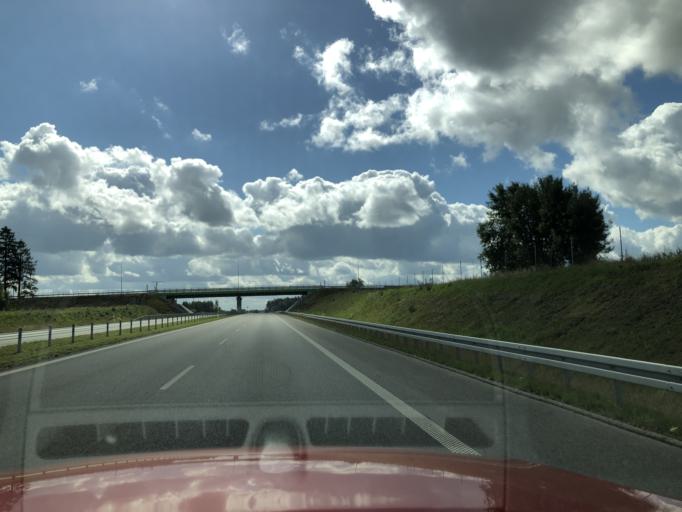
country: PL
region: West Pomeranian Voivodeship
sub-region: Powiat szczecinecki
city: Szczecinek
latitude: 53.6693
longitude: 16.7371
